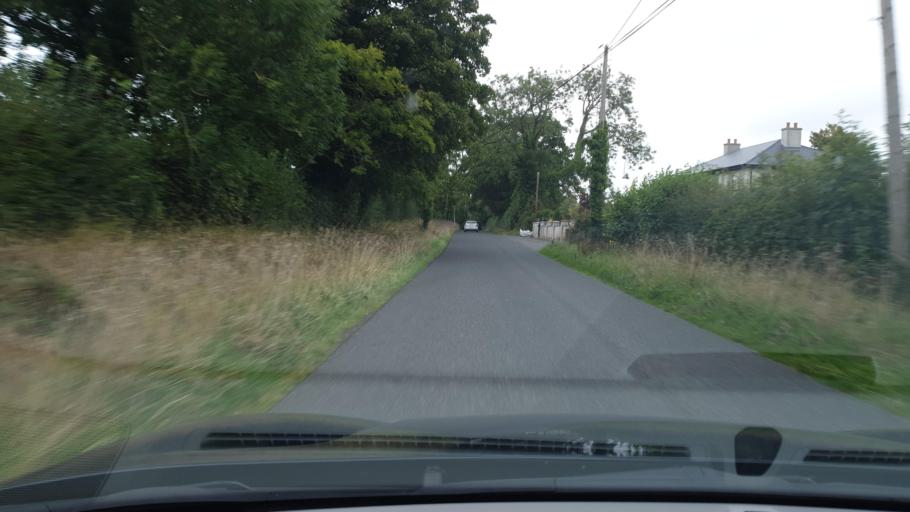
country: IE
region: Leinster
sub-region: An Mhi
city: Dunshaughlin
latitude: 53.5497
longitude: -6.5338
